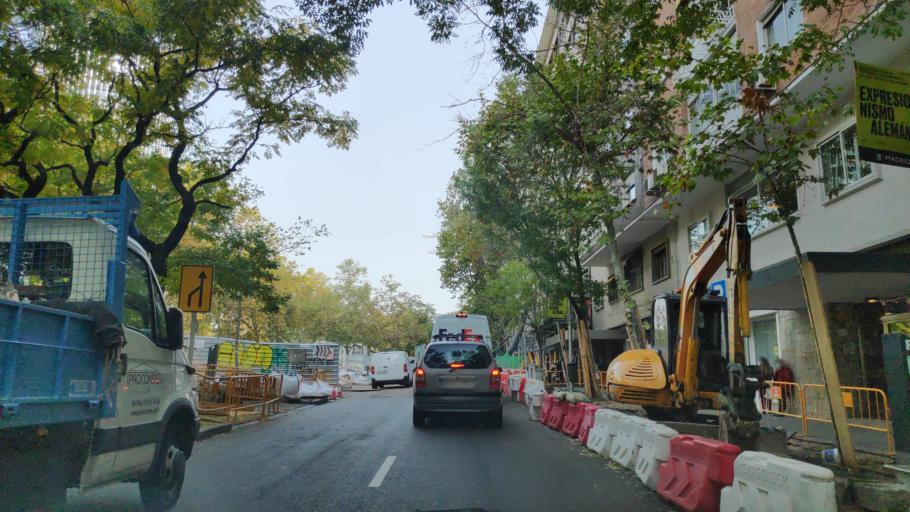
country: ES
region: Madrid
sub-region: Provincia de Madrid
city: Chamartin
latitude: 40.4496
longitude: -3.6904
